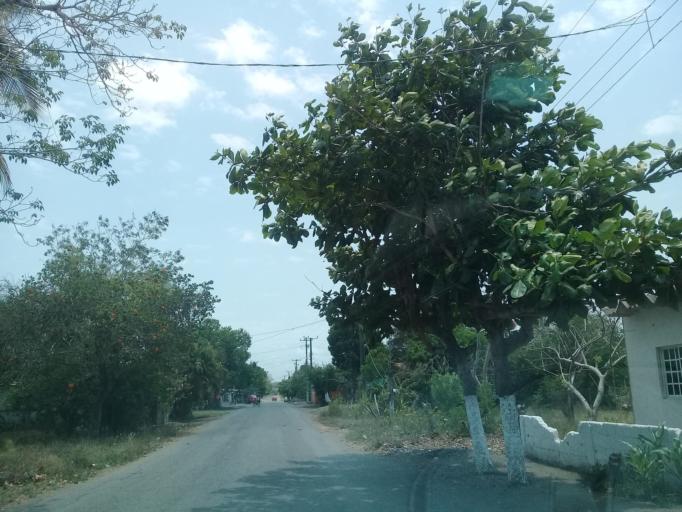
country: MX
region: Veracruz
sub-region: Veracruz
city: Delfino Victoria (Santa Fe)
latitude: 19.1741
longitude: -96.3010
